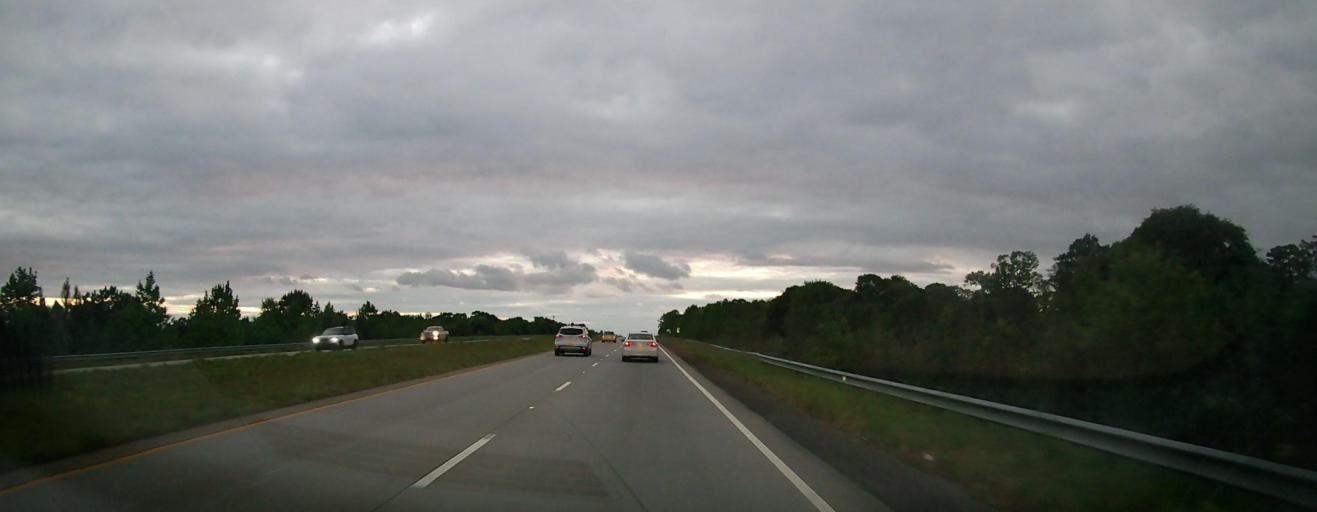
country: US
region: Georgia
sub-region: Jackson County
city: Arcade
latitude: 34.0741
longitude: -83.5607
